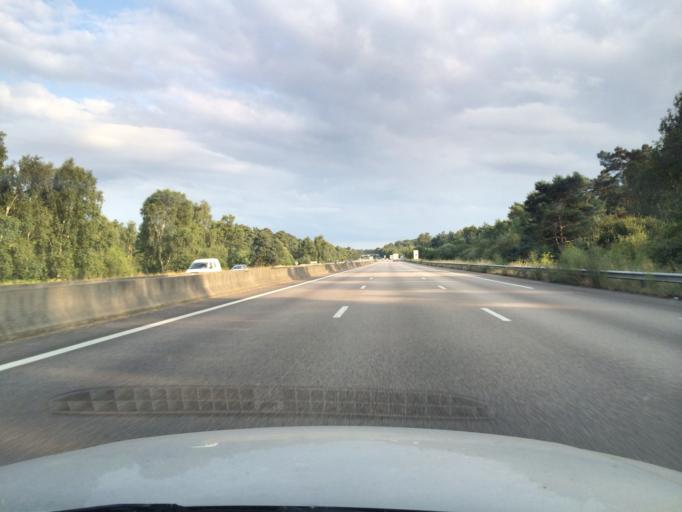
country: FR
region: Haute-Normandie
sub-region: Departement de l'Eure
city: Criquebeuf-sur-Seine
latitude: 49.2863
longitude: 1.1255
